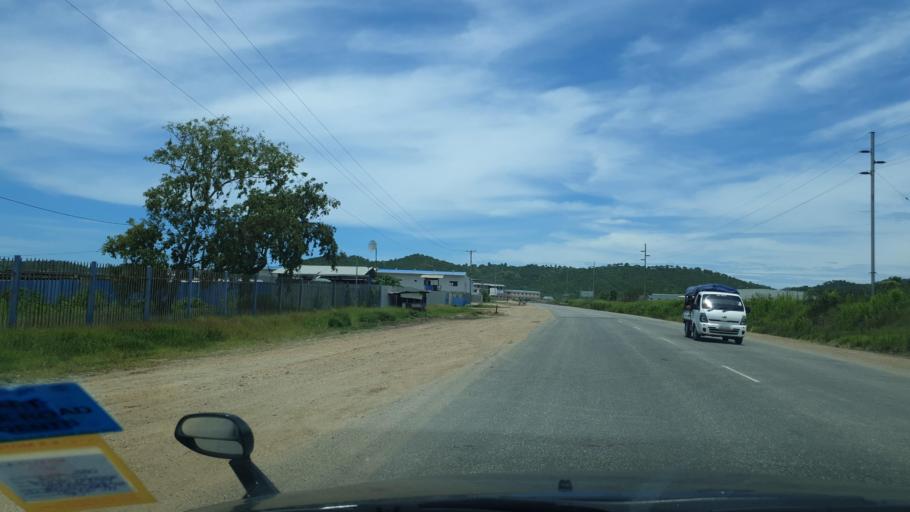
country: PG
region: National Capital
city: Port Moresby
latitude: -9.4195
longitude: 147.0848
